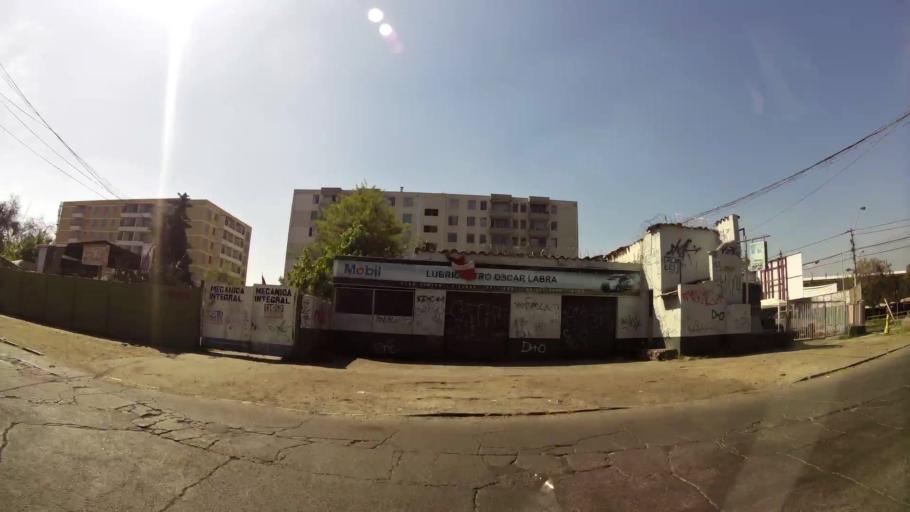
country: CL
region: Santiago Metropolitan
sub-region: Provincia de Santiago
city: Villa Presidente Frei, Nunoa, Santiago, Chile
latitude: -33.4871
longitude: -70.5862
